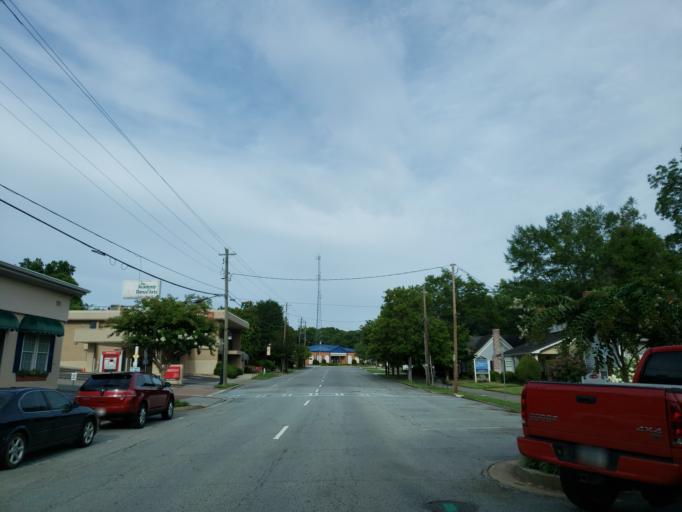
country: US
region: Georgia
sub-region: Cherokee County
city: Canton
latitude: 34.2367
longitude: -84.4894
